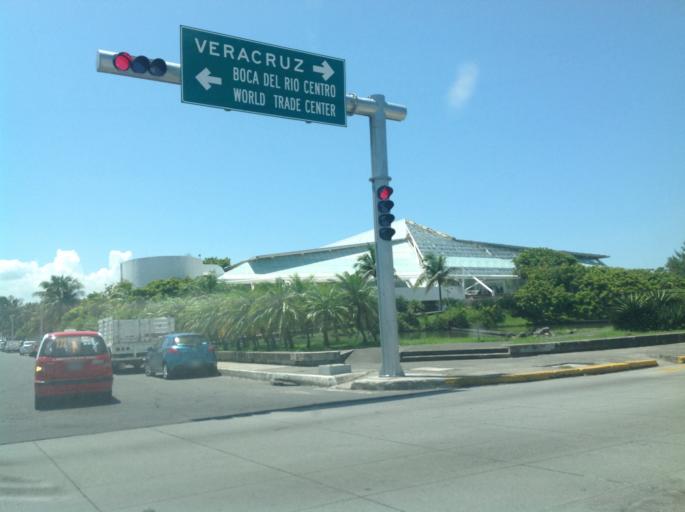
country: MX
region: Veracruz
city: Veracruz
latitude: 19.1597
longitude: -96.1092
